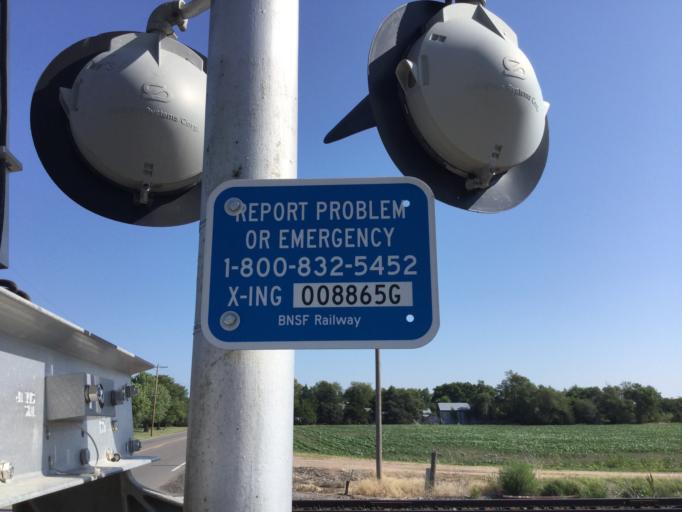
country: US
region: Kansas
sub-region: Reno County
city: Buhler
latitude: 38.0230
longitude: -97.6657
